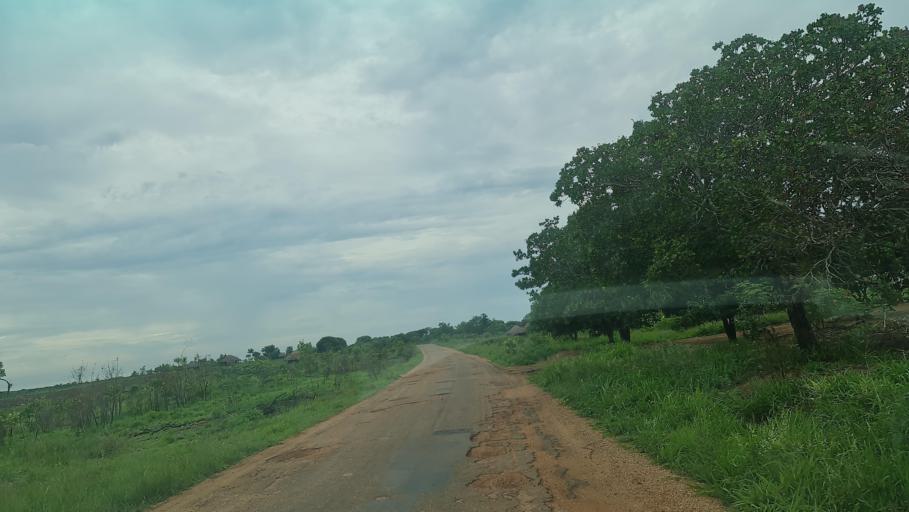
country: MW
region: Southern Region
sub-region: Nsanje District
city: Nsanje
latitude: -17.6882
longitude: 35.7309
